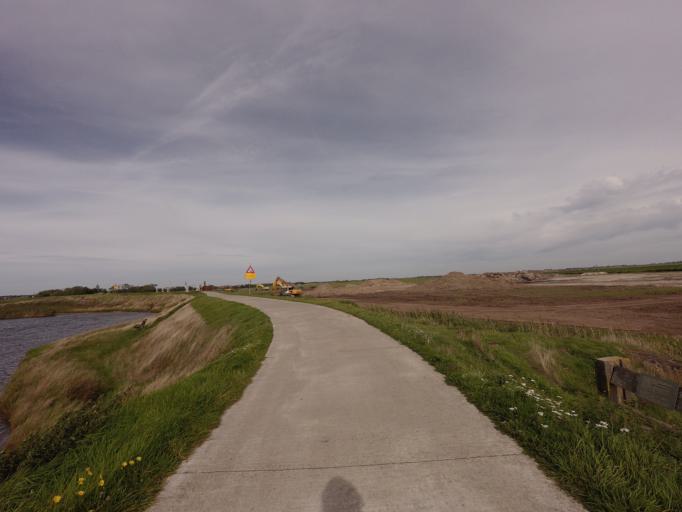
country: NL
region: North Holland
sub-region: Gemeente Texel
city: Den Burg
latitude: 53.0740
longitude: 4.7914
